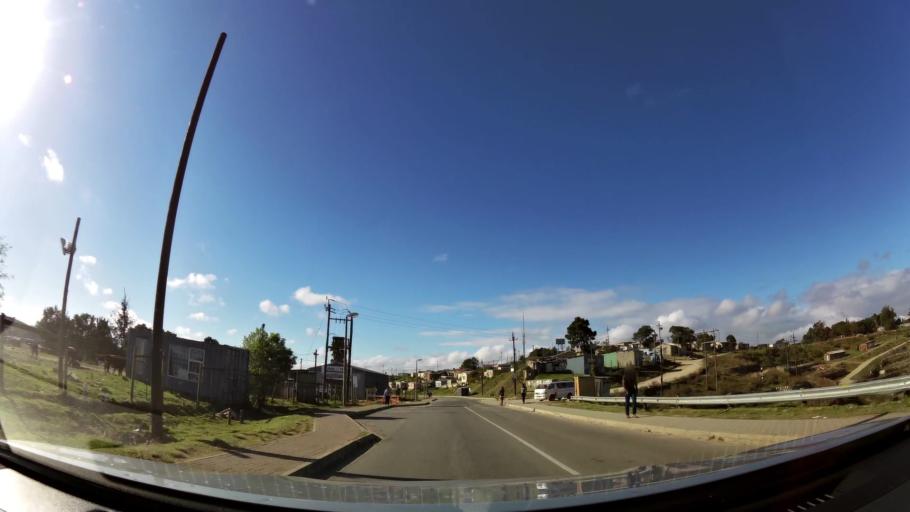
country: ZA
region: Western Cape
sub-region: Eden District Municipality
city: Knysna
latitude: -34.0283
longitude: 23.0689
